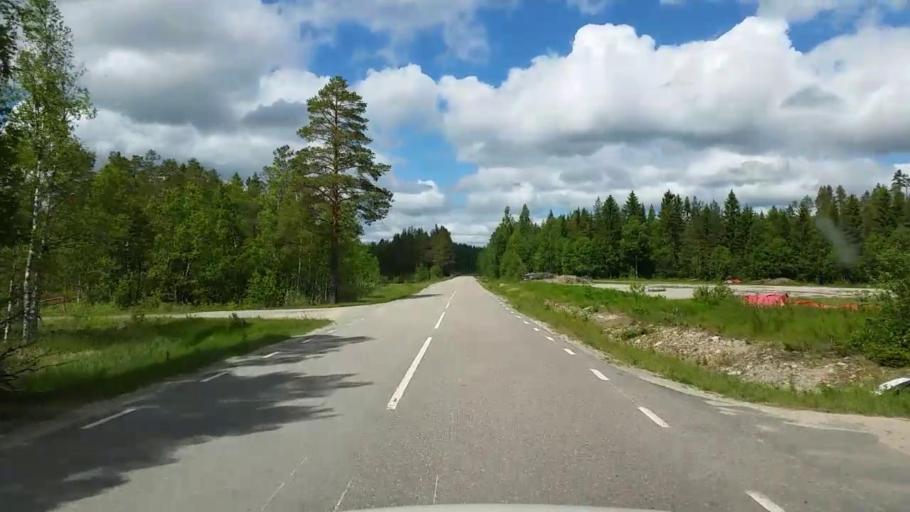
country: SE
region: Gaevleborg
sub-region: Bollnas Kommun
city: Vittsjo
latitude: 61.1488
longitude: 16.1615
